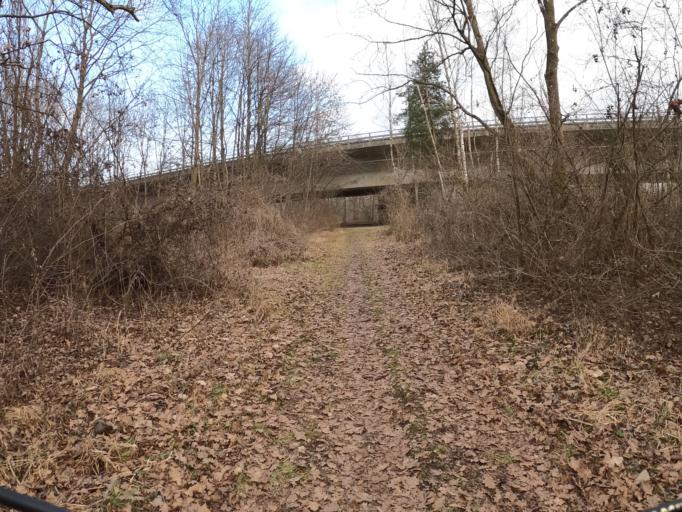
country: DE
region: Bavaria
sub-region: Swabia
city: Nersingen
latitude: 48.4406
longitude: 10.1108
